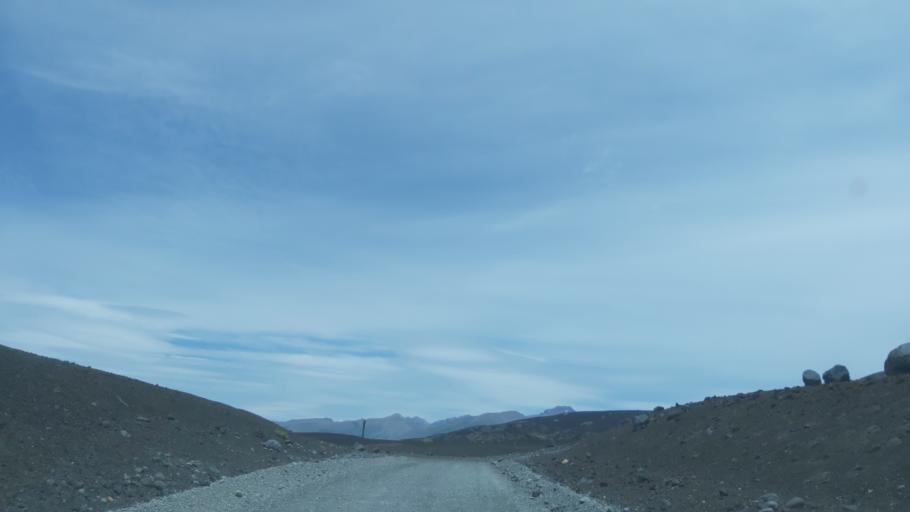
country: AR
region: Neuquen
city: Andacollo
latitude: -37.4195
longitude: -71.2891
